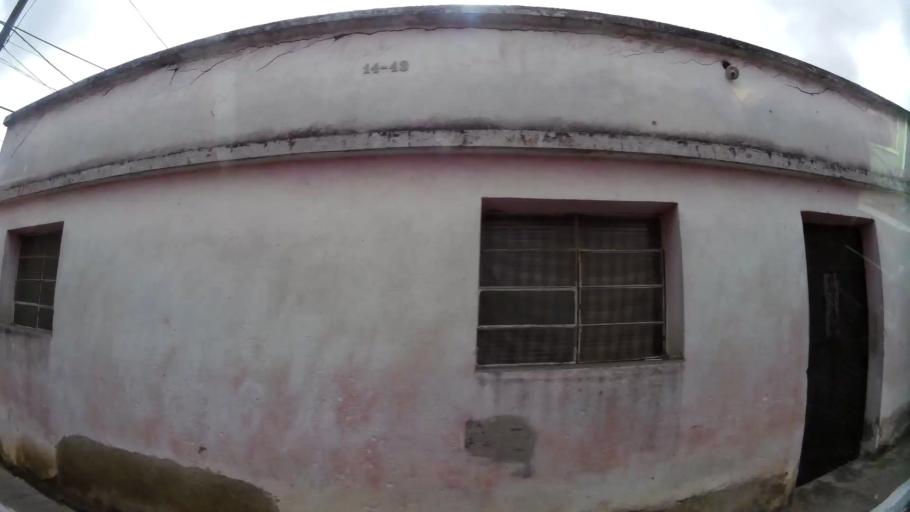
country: GT
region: Guatemala
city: Guatemala City
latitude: 14.6405
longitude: -90.5541
